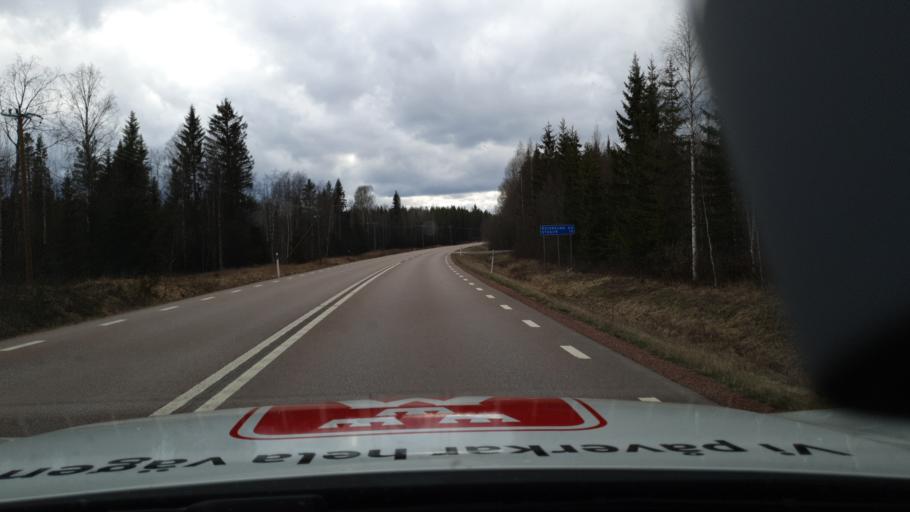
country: SE
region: Jaemtland
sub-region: Ragunda Kommun
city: Hammarstrand
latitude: 63.1728
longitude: 15.8852
